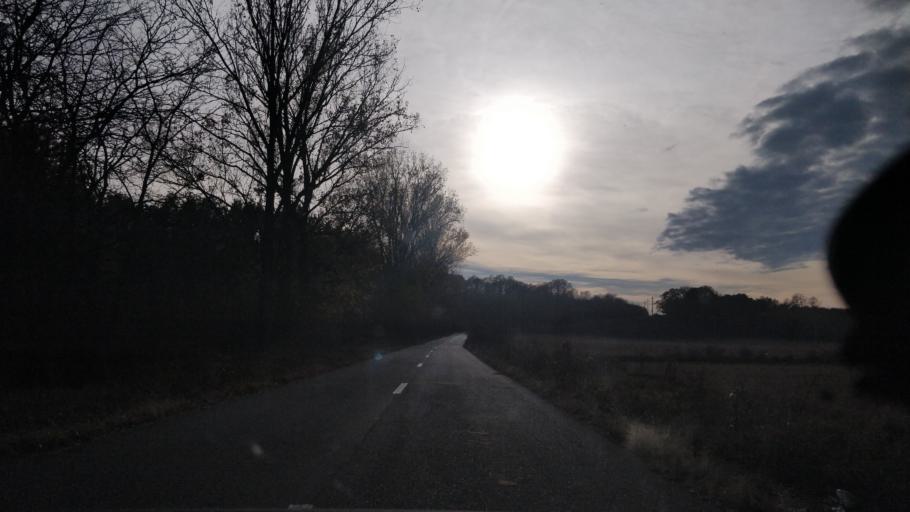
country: RO
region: Giurgiu
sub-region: Comuna Bucsani
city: Bucsani
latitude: 44.3381
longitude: 25.6615
